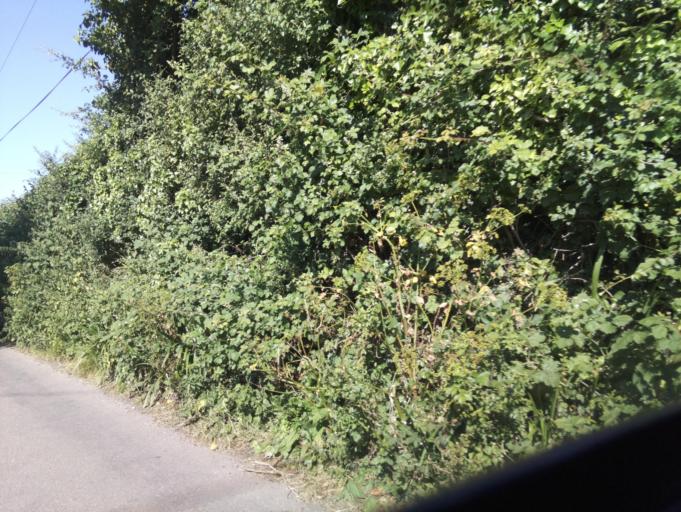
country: GB
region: England
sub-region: Devon
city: Dartmouth
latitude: 50.3918
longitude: -3.5672
